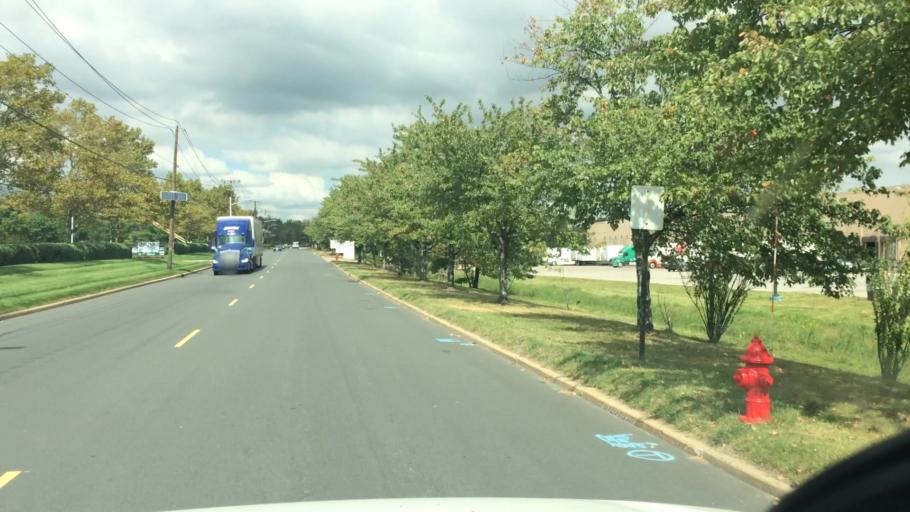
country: US
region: New Jersey
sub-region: Middlesex County
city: Fords
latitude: 40.5199
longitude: -74.3305
